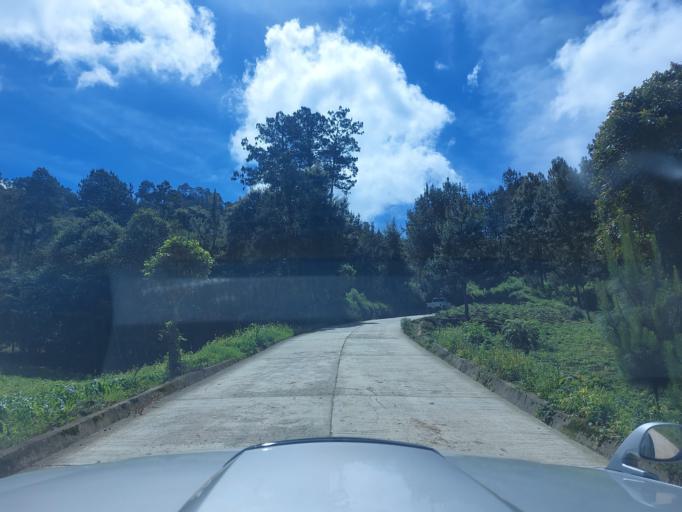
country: GT
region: Chimaltenango
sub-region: Municipio de San Juan Comalapa
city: Comalapa
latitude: 14.7529
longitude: -90.8681
